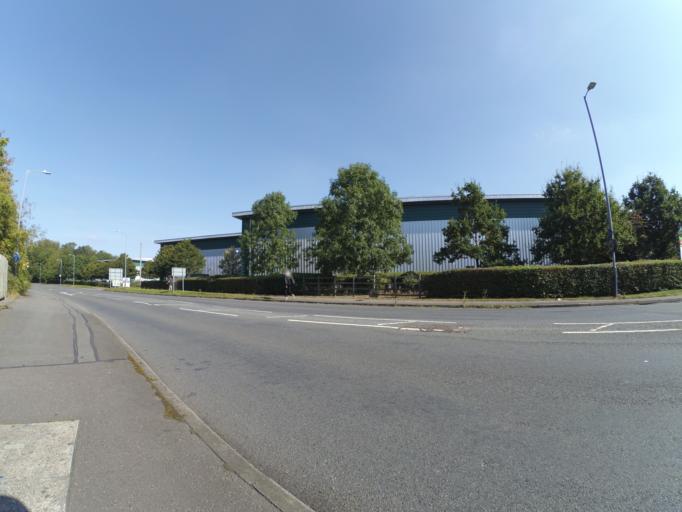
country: GB
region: England
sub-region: Warwickshire
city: Rugby
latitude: 52.3933
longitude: -1.2636
